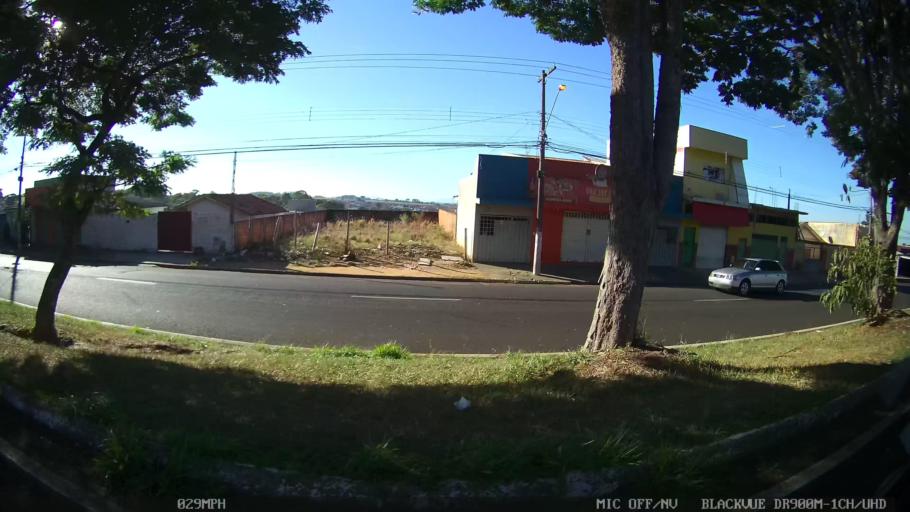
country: BR
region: Sao Paulo
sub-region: Franca
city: Franca
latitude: -20.5784
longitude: -47.3765
